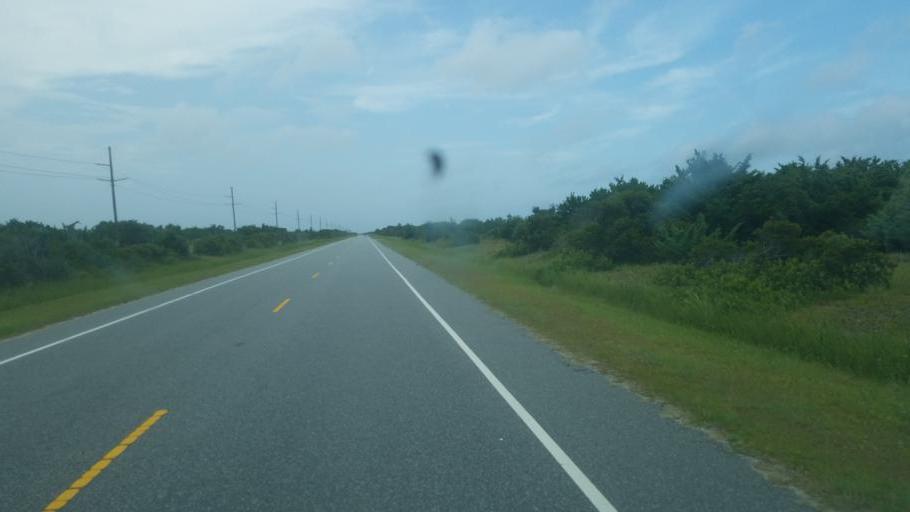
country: US
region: North Carolina
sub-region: Dare County
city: Buxton
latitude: 35.4094
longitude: -75.4884
